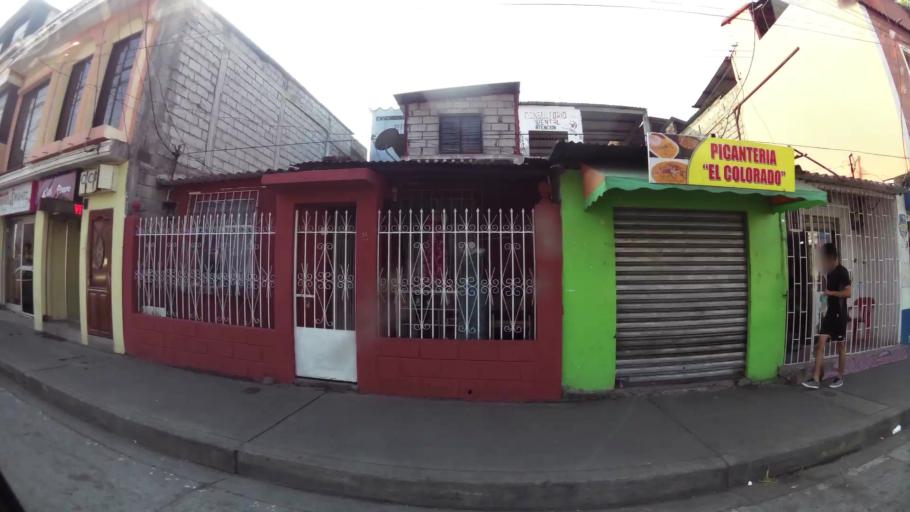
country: EC
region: Guayas
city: Eloy Alfaro
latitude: -2.1259
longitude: -79.8970
